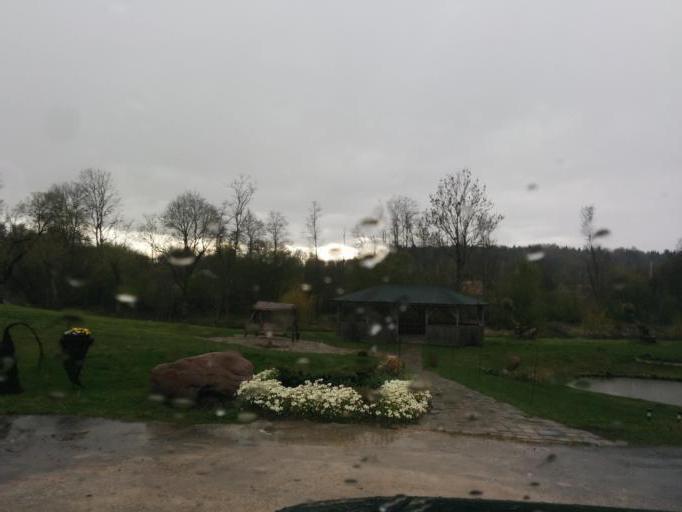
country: LV
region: Lecava
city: Iecava
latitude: 56.6217
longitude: 24.1886
